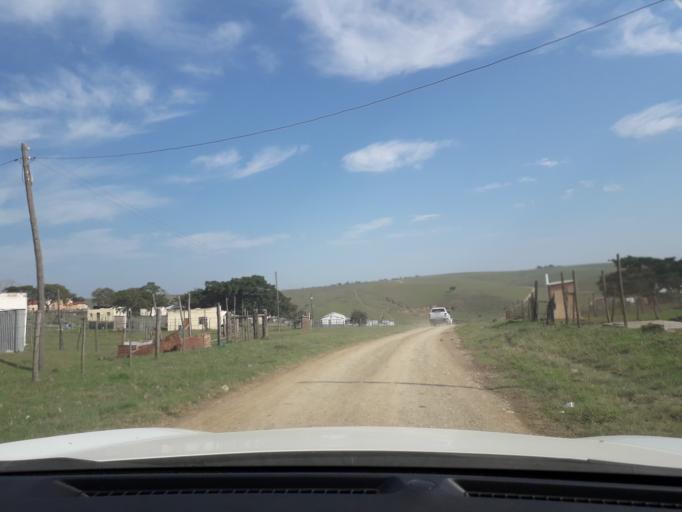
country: ZA
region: Eastern Cape
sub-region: Buffalo City Metropolitan Municipality
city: Bhisho
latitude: -33.0049
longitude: 27.3339
